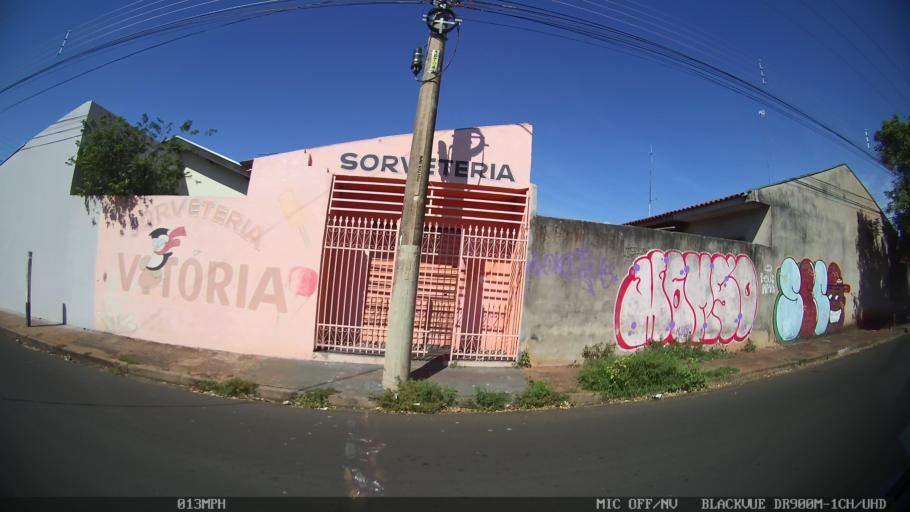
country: BR
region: Sao Paulo
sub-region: Sao Jose Do Rio Preto
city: Sao Jose do Rio Preto
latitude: -20.7668
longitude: -49.4000
